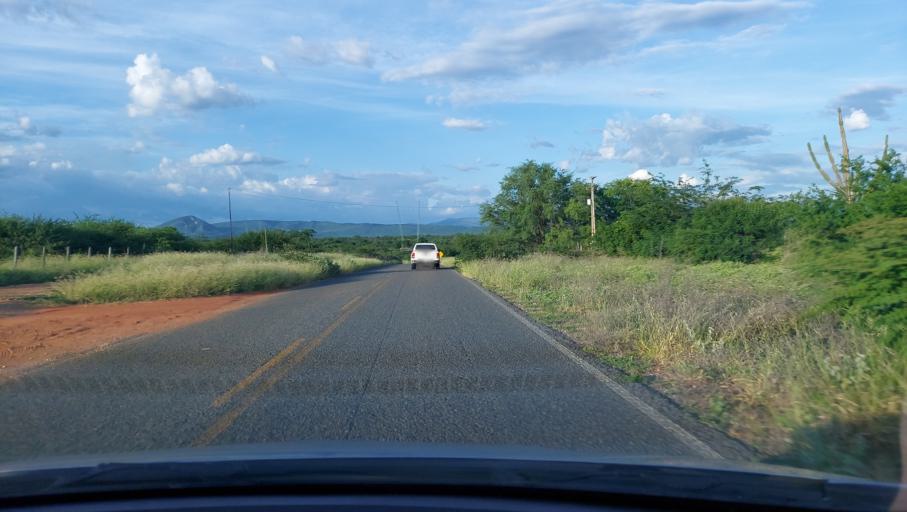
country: BR
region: Bahia
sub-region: Oliveira Dos Brejinhos
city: Beira Rio
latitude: -12.1979
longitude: -42.5380
